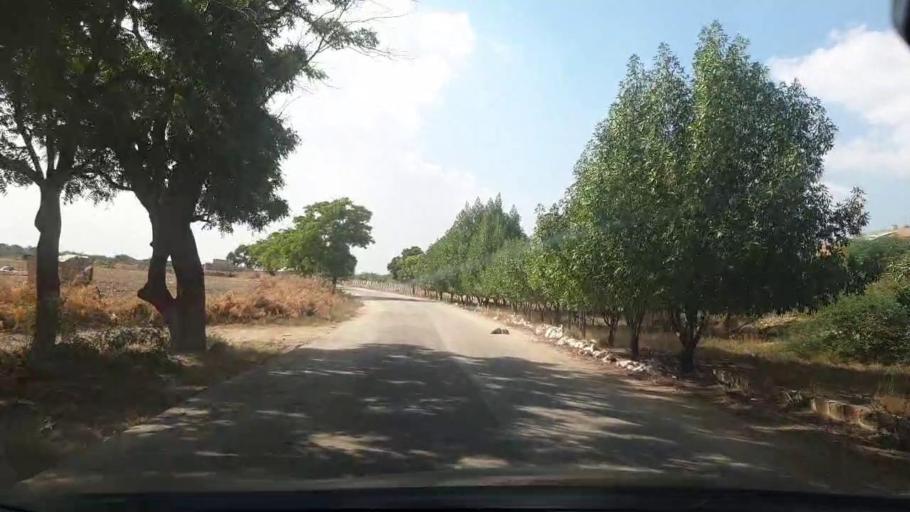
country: PK
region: Sindh
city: Malir Cantonment
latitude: 25.0260
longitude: 67.3600
